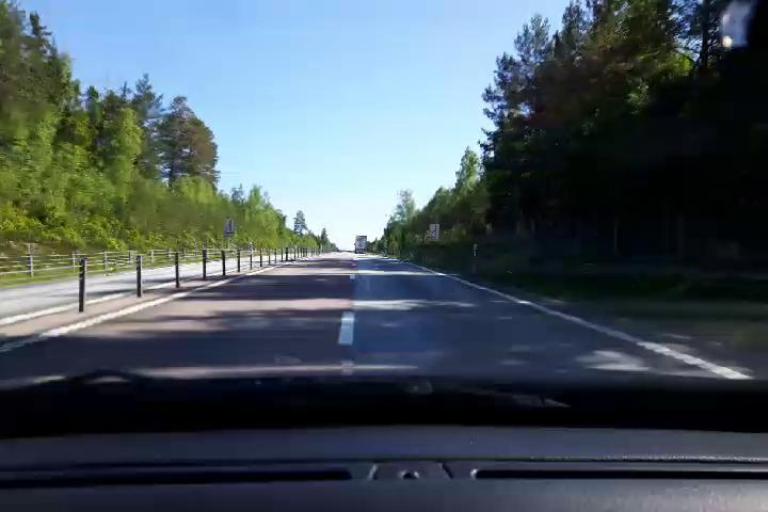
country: SE
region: Gaevleborg
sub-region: Soderhamns Kommun
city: Soderhamn
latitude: 61.2689
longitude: 17.0277
